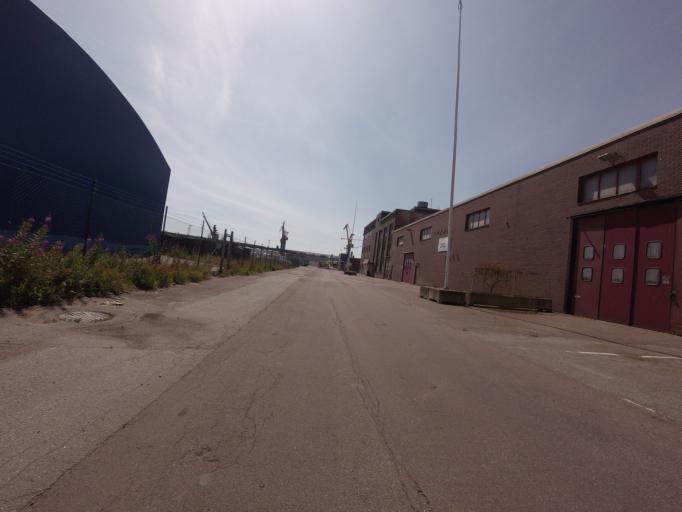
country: SE
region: Skane
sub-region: Landskrona
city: Landskrona
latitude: 55.8611
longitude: 12.8308
